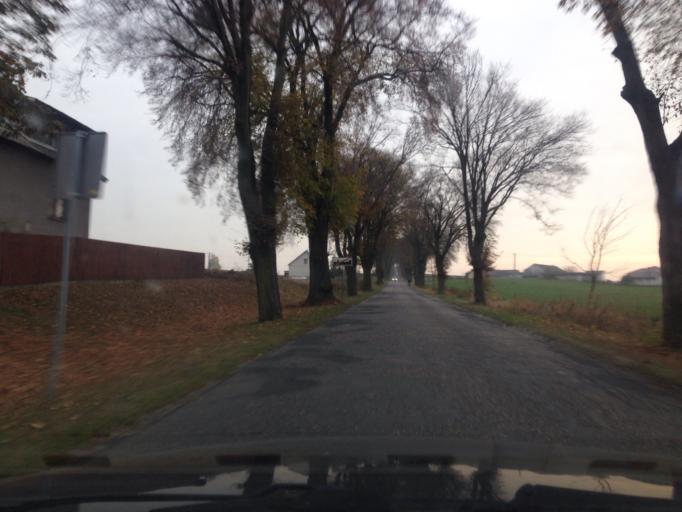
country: PL
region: Kujawsko-Pomorskie
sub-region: Powiat brodnicki
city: Gorzno
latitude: 53.2274
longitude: 19.6333
